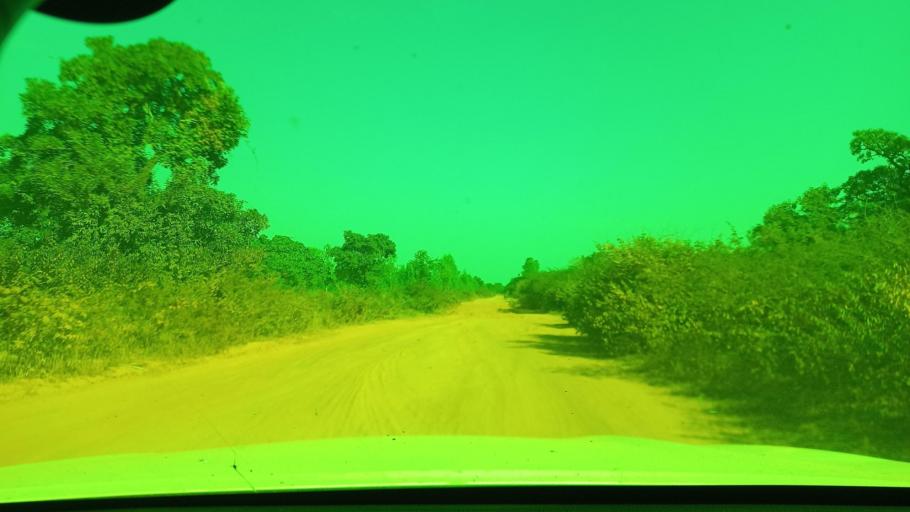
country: ML
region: Bamako
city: Bamako
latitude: 12.3961
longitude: -7.9771
